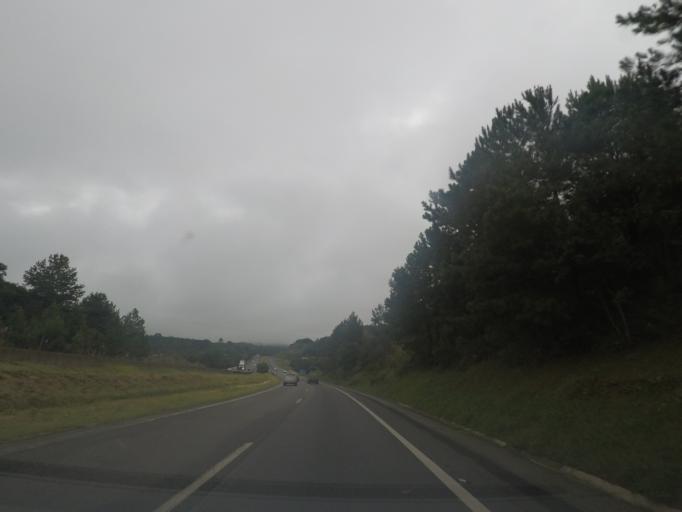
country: BR
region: Parana
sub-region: Campina Grande Do Sul
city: Campina Grande do Sul
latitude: -25.2558
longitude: -48.9128
